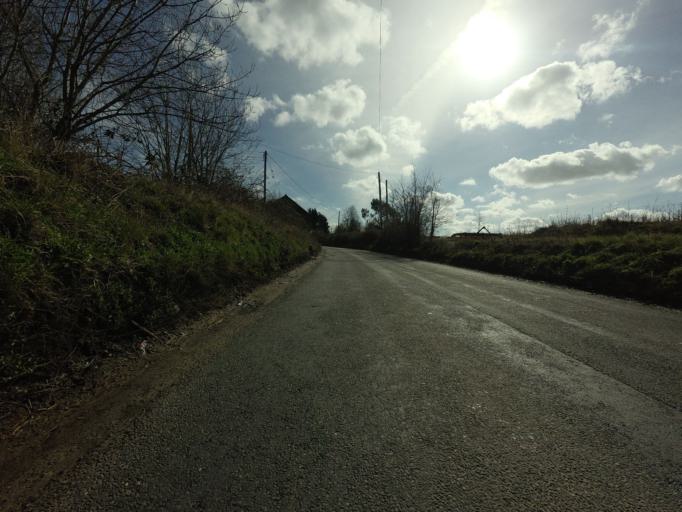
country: GB
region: England
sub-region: Kent
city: Swanley
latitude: 51.3846
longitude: 0.1440
